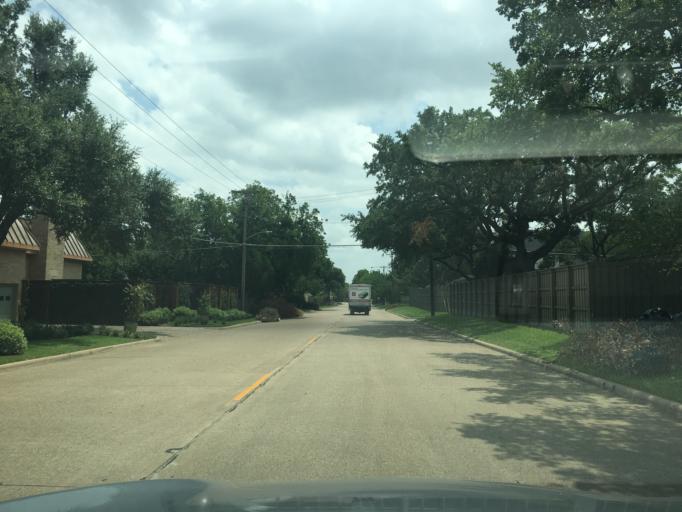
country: US
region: Texas
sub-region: Dallas County
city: University Park
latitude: 32.8974
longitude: -96.8296
